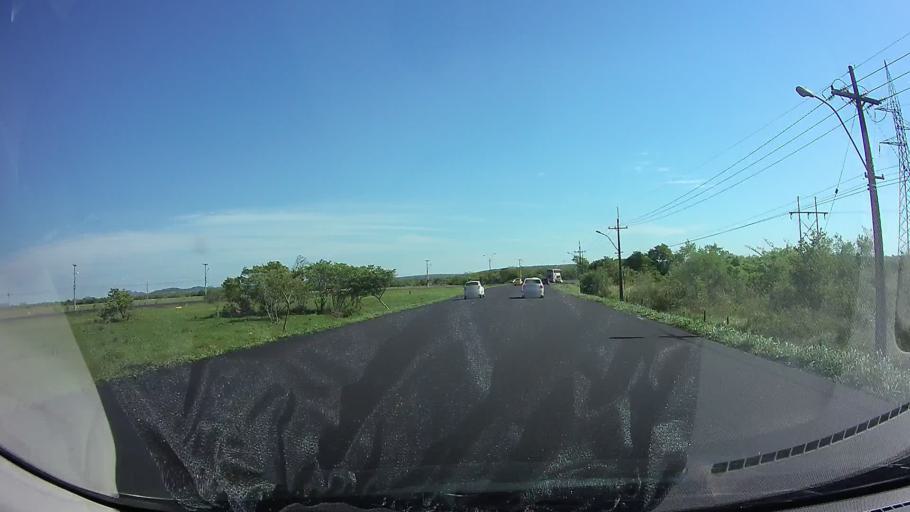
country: PY
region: Central
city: Ypacarai
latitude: -25.3862
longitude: -57.2661
